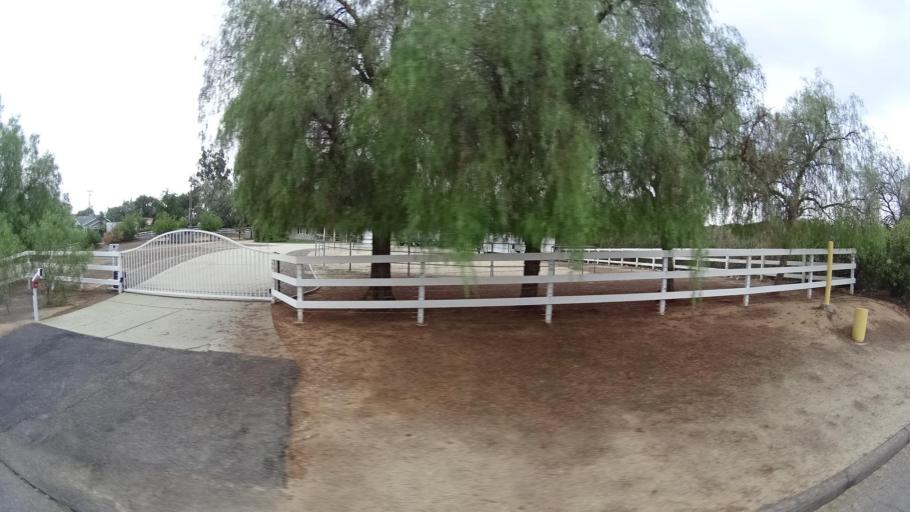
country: US
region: California
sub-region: San Diego County
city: Ramona
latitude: 33.0465
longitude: -116.8798
